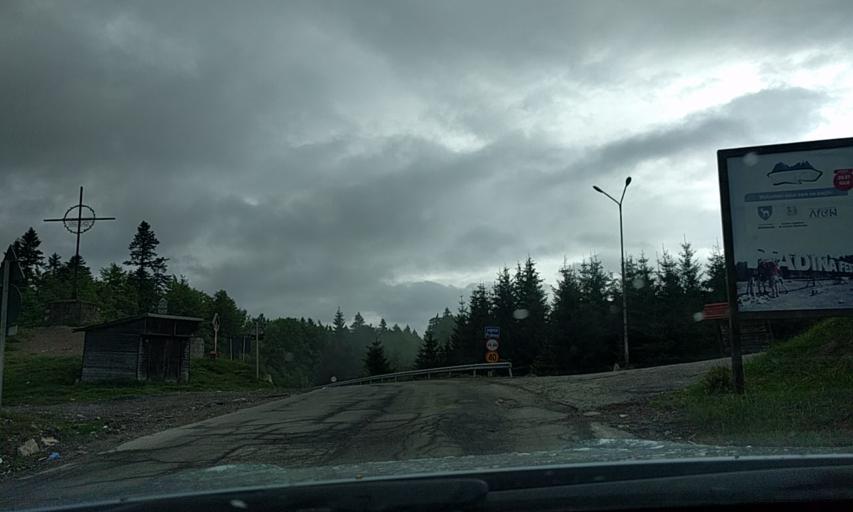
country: RO
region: Prahova
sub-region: Oras Sinaia
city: Sinaia
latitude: 45.3079
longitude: 25.5224
